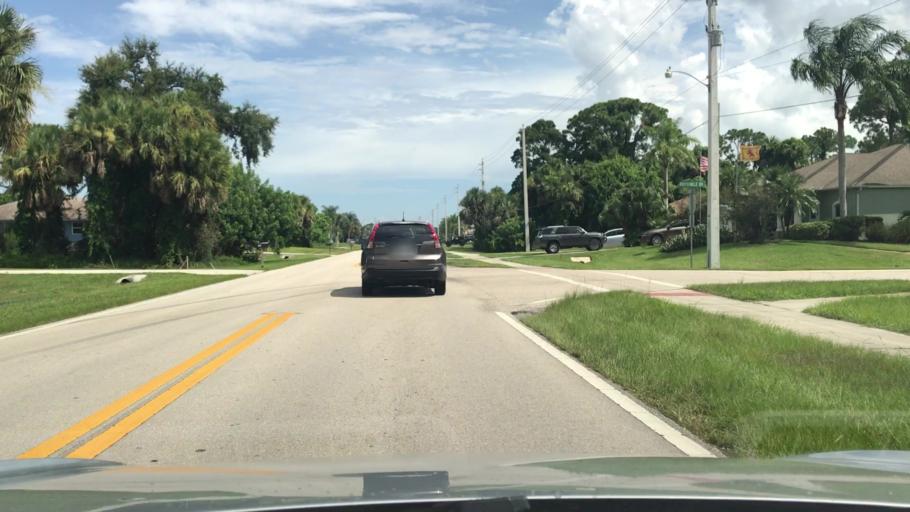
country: US
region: Florida
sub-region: Indian River County
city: Sebastian
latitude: 27.7631
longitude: -80.4751
